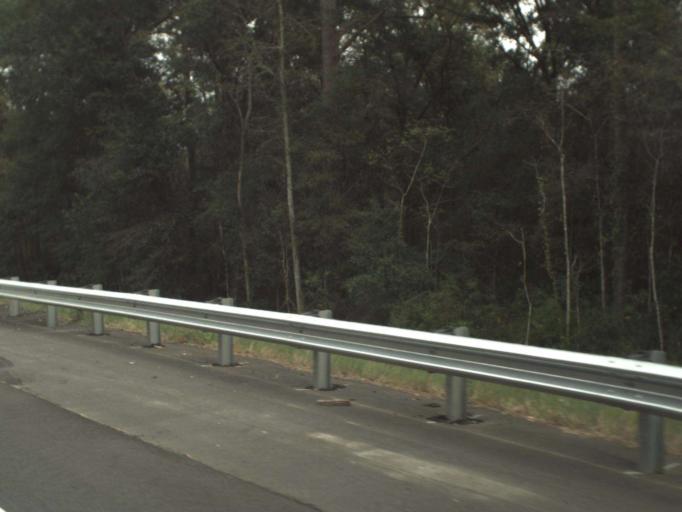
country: US
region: Florida
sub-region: Calhoun County
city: Blountstown
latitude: 30.4977
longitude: -85.0424
